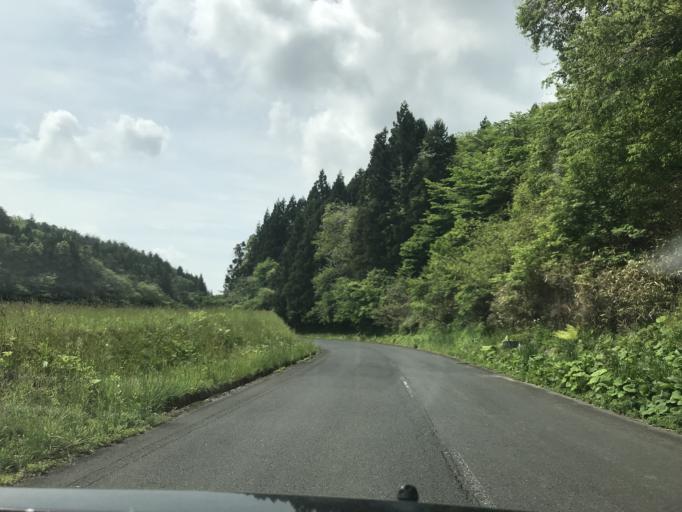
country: JP
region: Iwate
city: Ichinoseki
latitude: 38.8816
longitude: 140.9748
